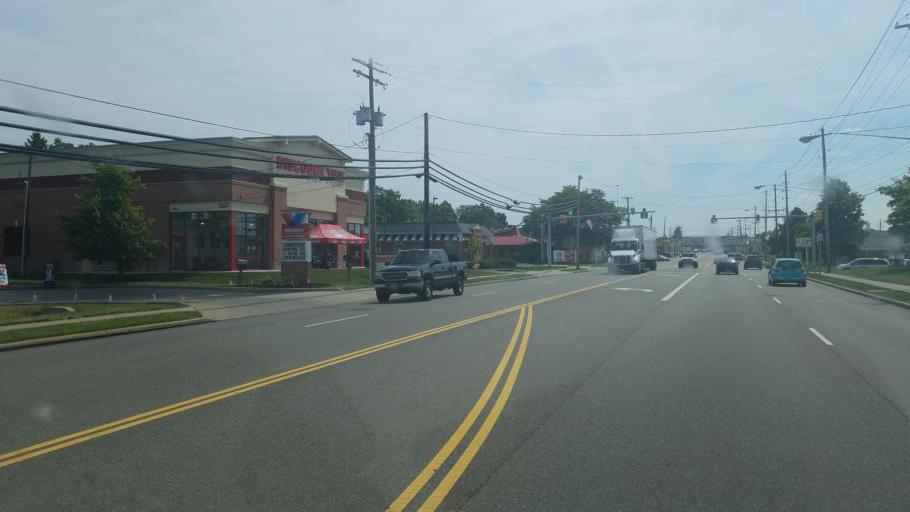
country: US
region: Ohio
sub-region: Summit County
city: Macedonia
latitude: 41.3139
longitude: -81.5184
